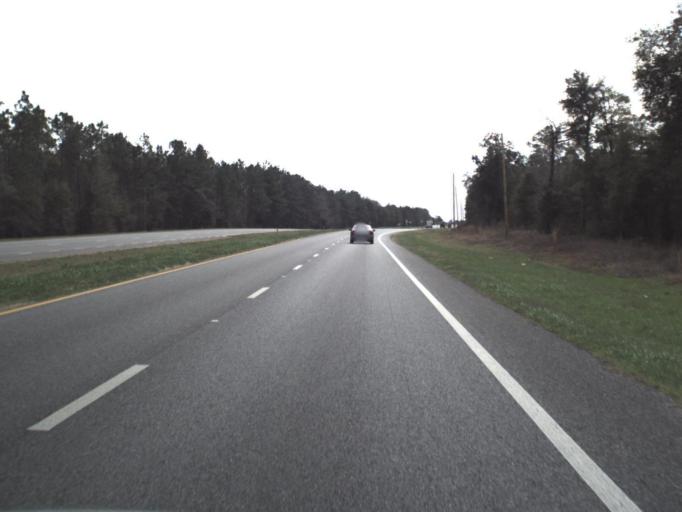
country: US
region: Florida
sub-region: Washington County
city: Chipley
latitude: 30.7428
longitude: -85.3854
